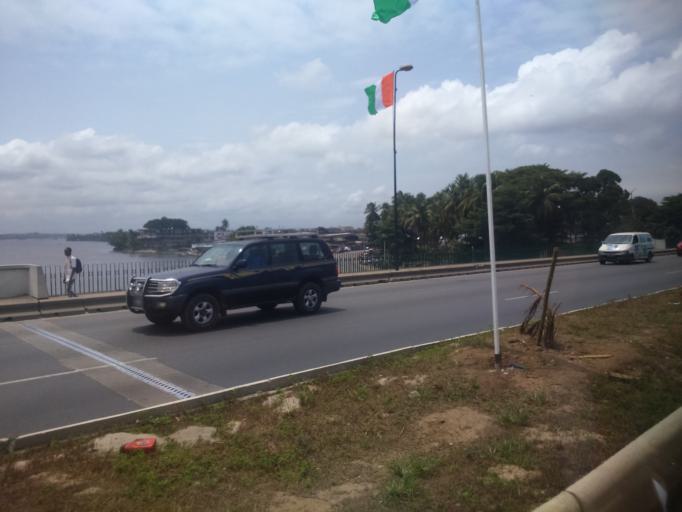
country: CI
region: Lagunes
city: Abidjan
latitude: 5.3142
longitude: -4.0092
